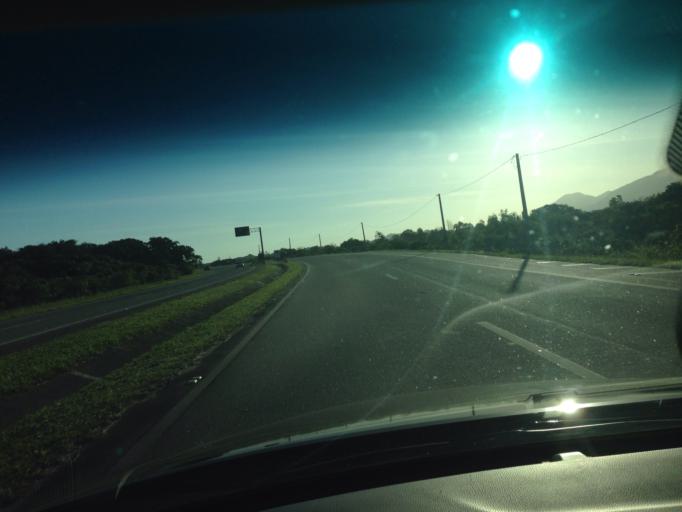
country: BR
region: Espirito Santo
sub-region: Guarapari
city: Guarapari
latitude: -20.5852
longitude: -40.4225
